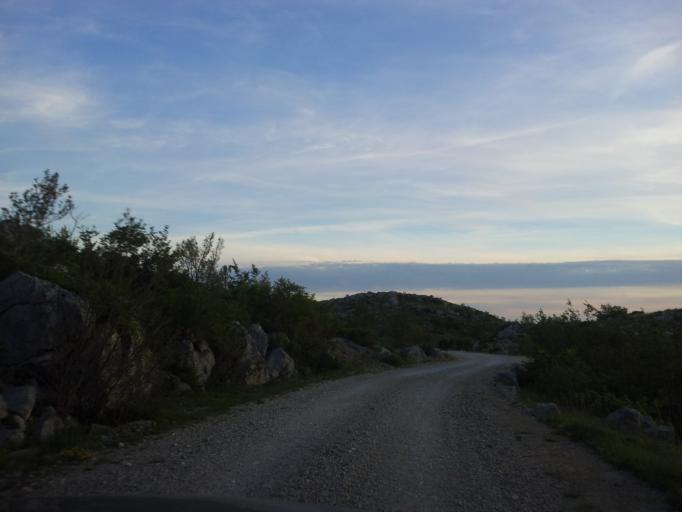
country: HR
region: Zadarska
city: Obrovac
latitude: 44.2595
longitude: 15.6386
